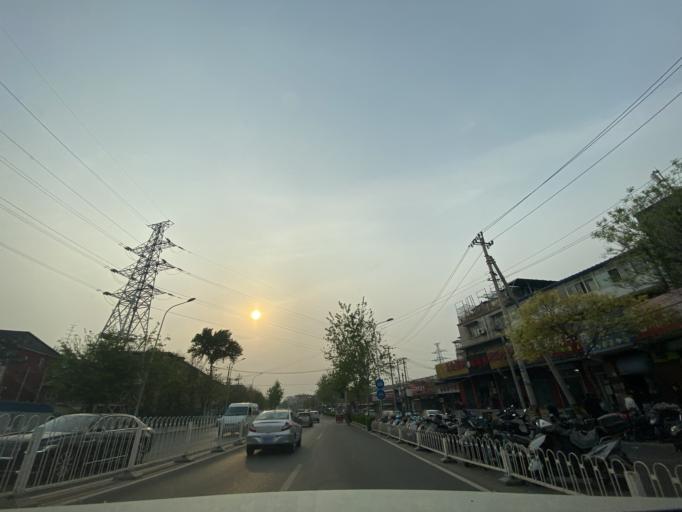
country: CN
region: Beijing
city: Sijiqing
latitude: 39.9275
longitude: 116.2664
